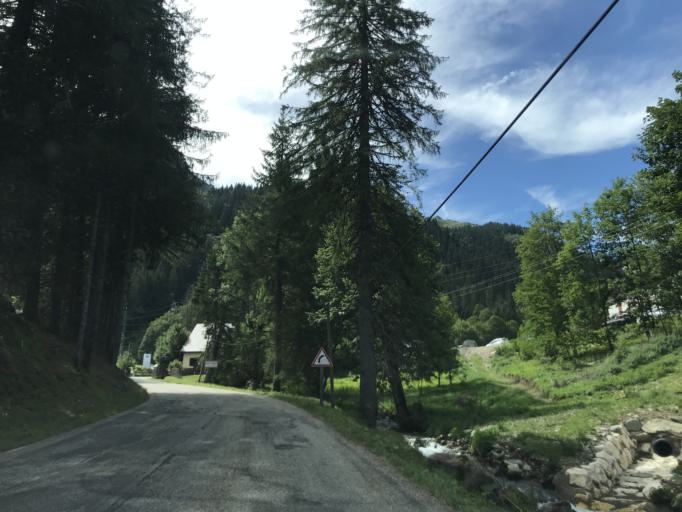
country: FR
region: Rhone-Alpes
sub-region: Departement de l'Isere
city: Theys
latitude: 45.2811
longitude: 6.0736
